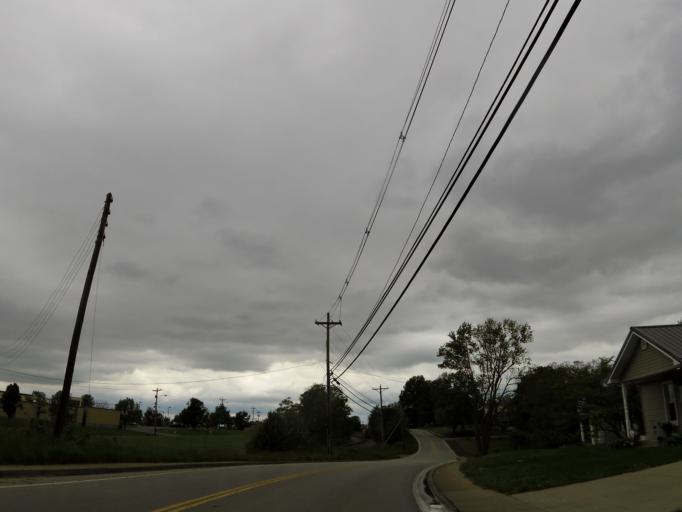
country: US
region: Kentucky
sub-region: Grant County
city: Williamstown
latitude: 38.6467
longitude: -84.5633
